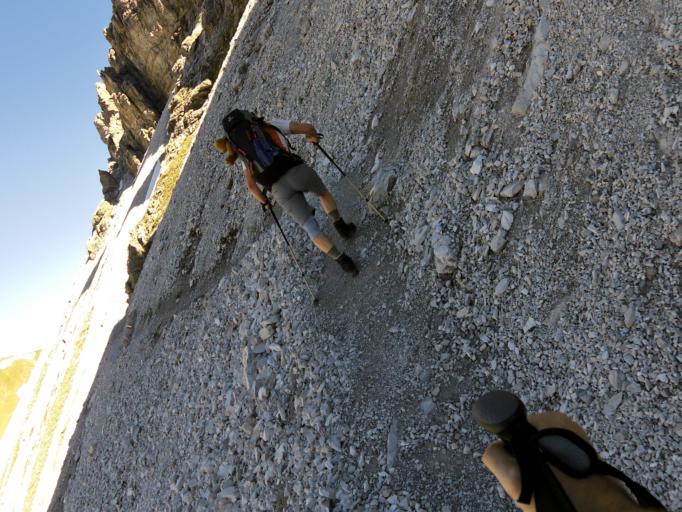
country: AT
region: Tyrol
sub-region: Politischer Bezirk Innsbruck Land
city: Neustift im Stubaital
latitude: 47.1406
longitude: 11.2744
